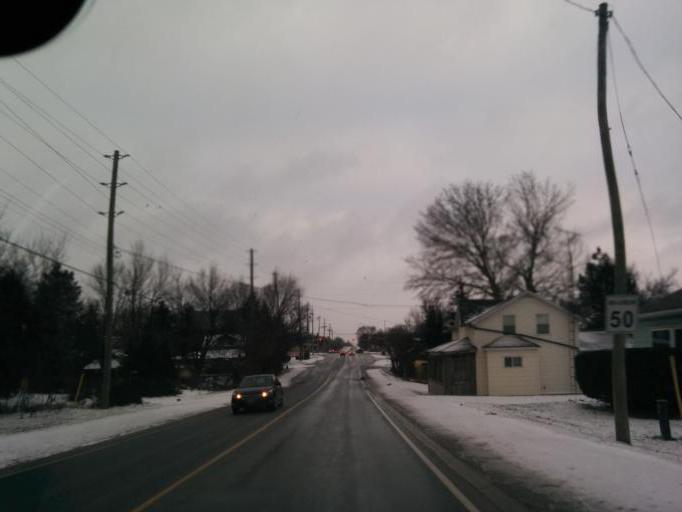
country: CA
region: Ontario
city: Orangeville
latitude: 43.8587
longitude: -79.9975
